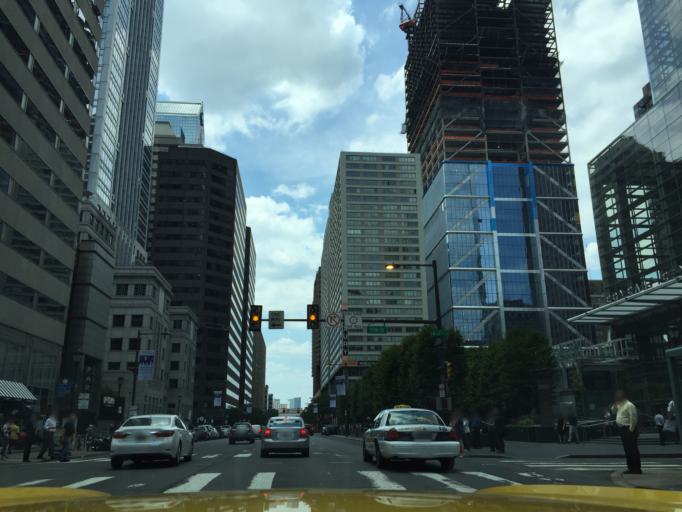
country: US
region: Pennsylvania
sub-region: Philadelphia County
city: Philadelphia
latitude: 39.9540
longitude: -75.1679
